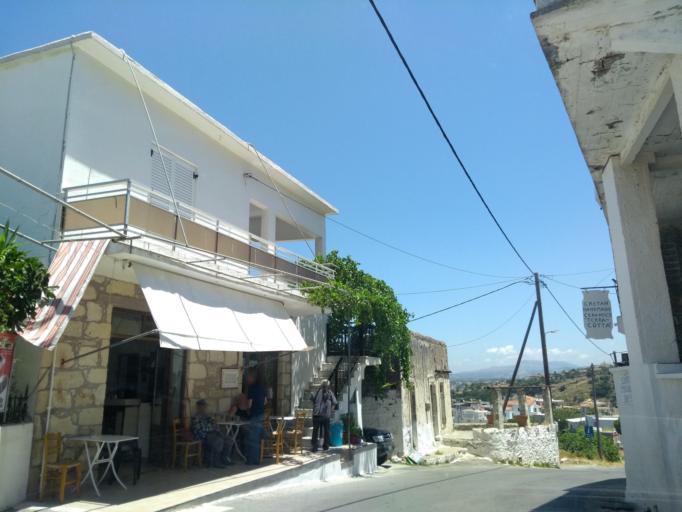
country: GR
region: Crete
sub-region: Nomos Chanias
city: Georgioupolis
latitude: 35.3140
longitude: 24.2955
